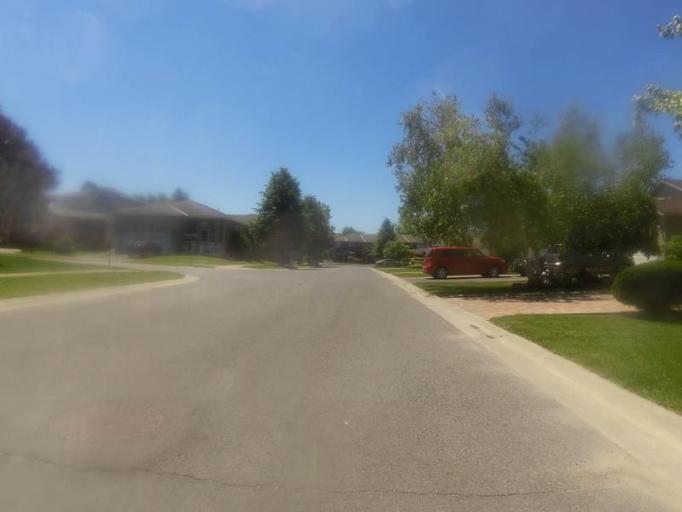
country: CA
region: Ontario
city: Kingston
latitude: 44.2615
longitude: -76.5561
